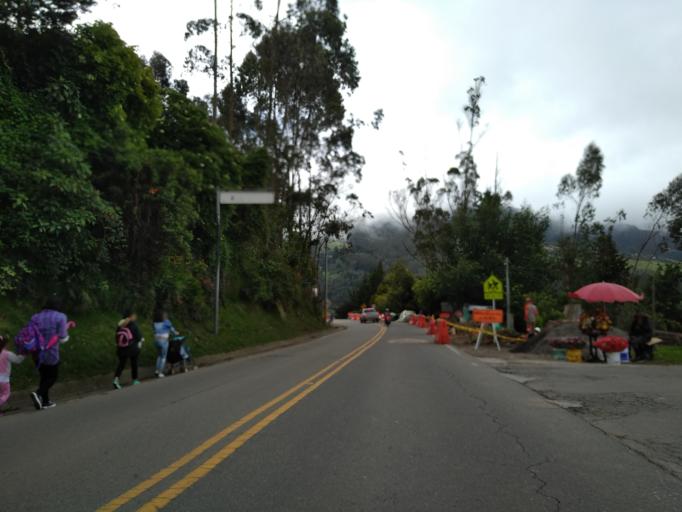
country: CO
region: Bogota D.C.
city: Barrio San Luis
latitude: 4.6622
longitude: -74.0098
